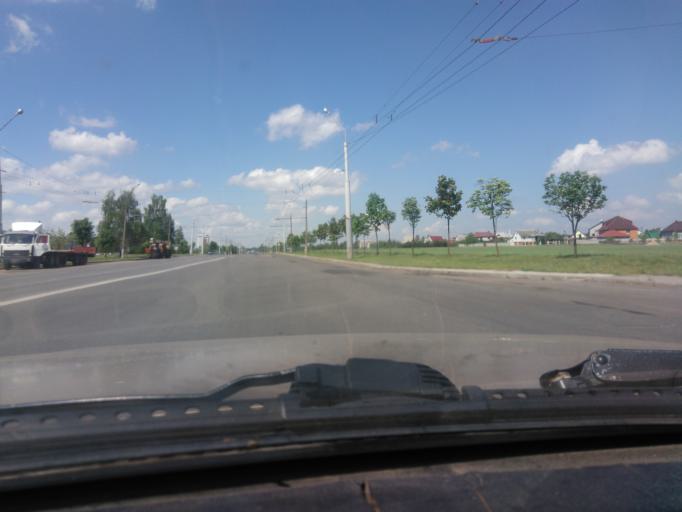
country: BY
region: Mogilev
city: Palykavichy Pyershyya
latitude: 53.9614
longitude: 30.3590
